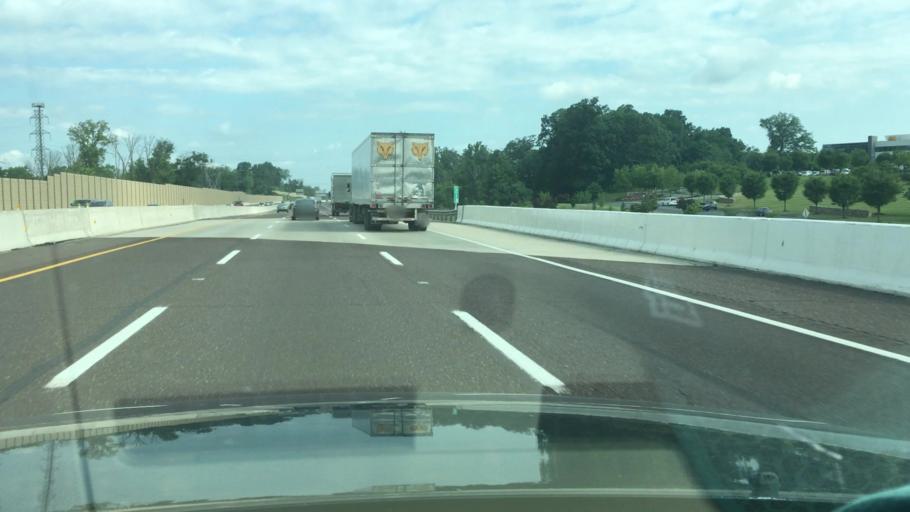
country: US
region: Pennsylvania
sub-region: Montgomery County
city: Blue Bell
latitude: 40.1370
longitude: -75.2878
